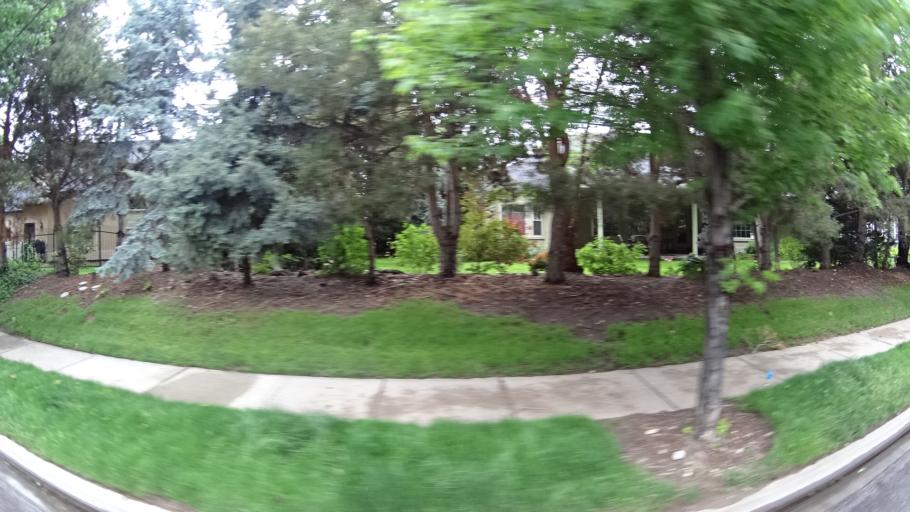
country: US
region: Idaho
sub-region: Ada County
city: Eagle
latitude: 43.6856
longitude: -116.3589
